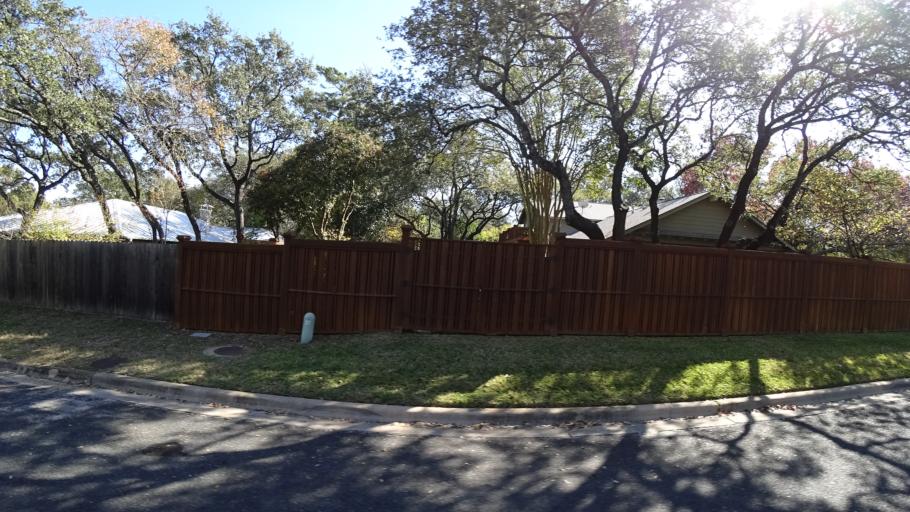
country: US
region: Texas
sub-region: Williamson County
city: Jollyville
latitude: 30.3690
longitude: -97.7729
